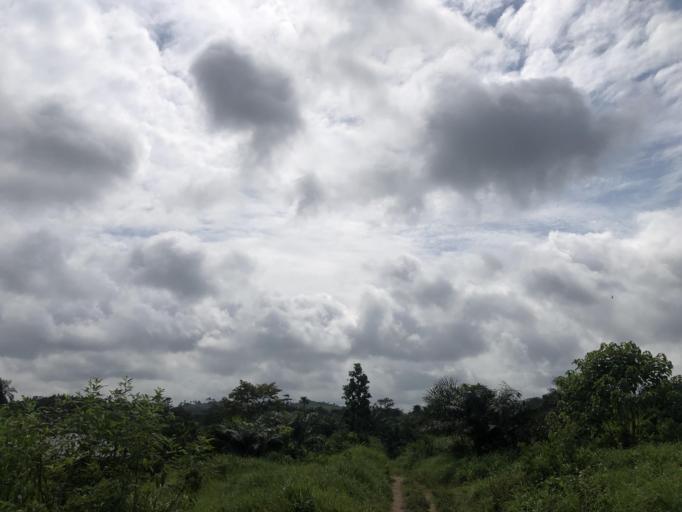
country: SL
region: Eastern Province
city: Kailahun
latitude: 8.2885
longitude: -10.5556
